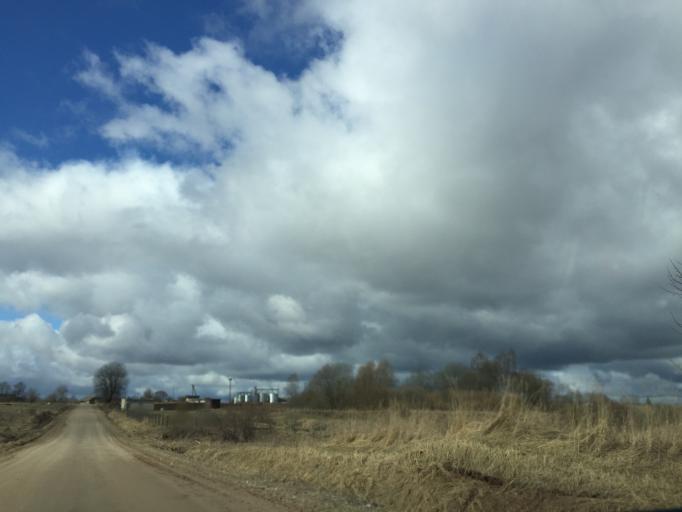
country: LV
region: Akniste
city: Akniste
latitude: 56.1007
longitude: 25.9710
